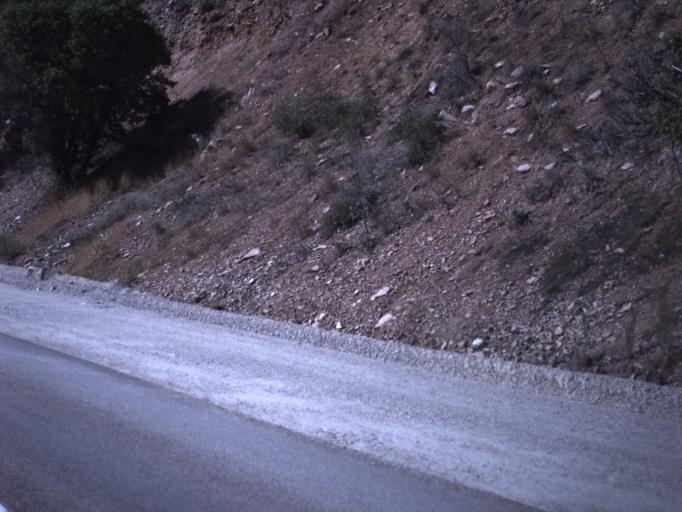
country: US
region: Utah
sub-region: Wasatch County
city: Heber
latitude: 40.4111
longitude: -111.3200
